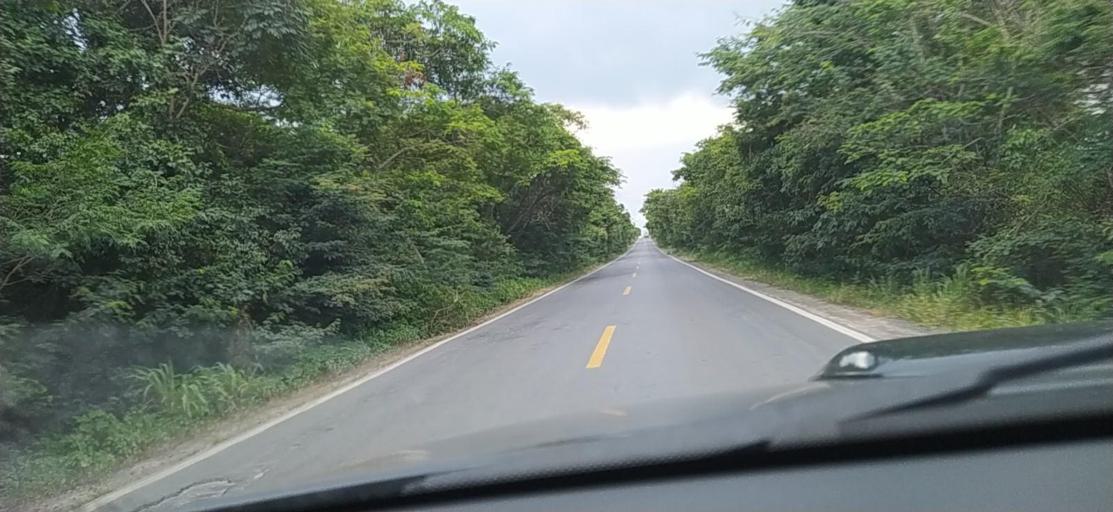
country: BR
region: Minas Gerais
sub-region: Francisco Sa
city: Francisco Sa
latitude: -16.2318
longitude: -43.6147
